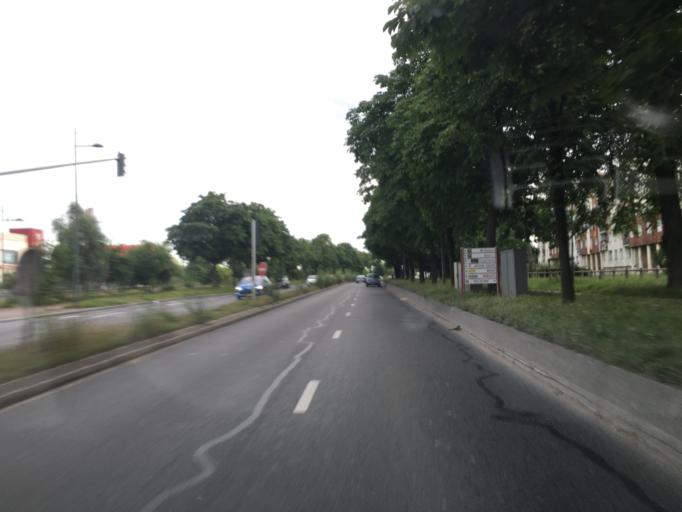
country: FR
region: Ile-de-France
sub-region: Departement du Val-de-Marne
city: Bonneuil-sur-Marne
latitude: 48.7711
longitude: 2.4899
